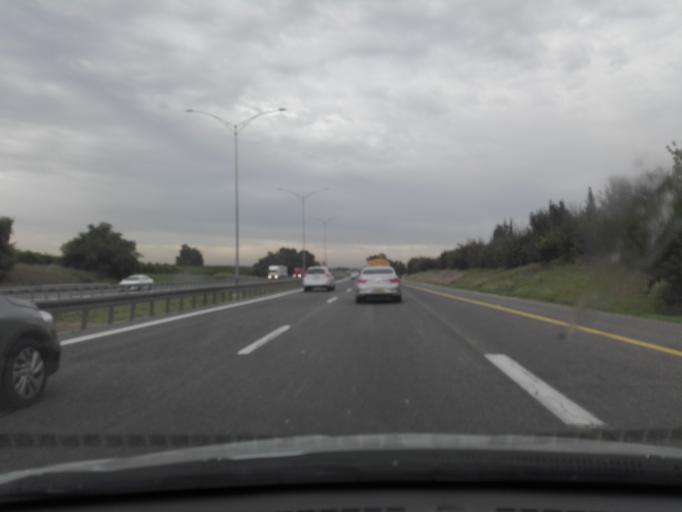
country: IL
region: Central District
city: Mazkeret Batya
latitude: 31.8767
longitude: 34.8766
